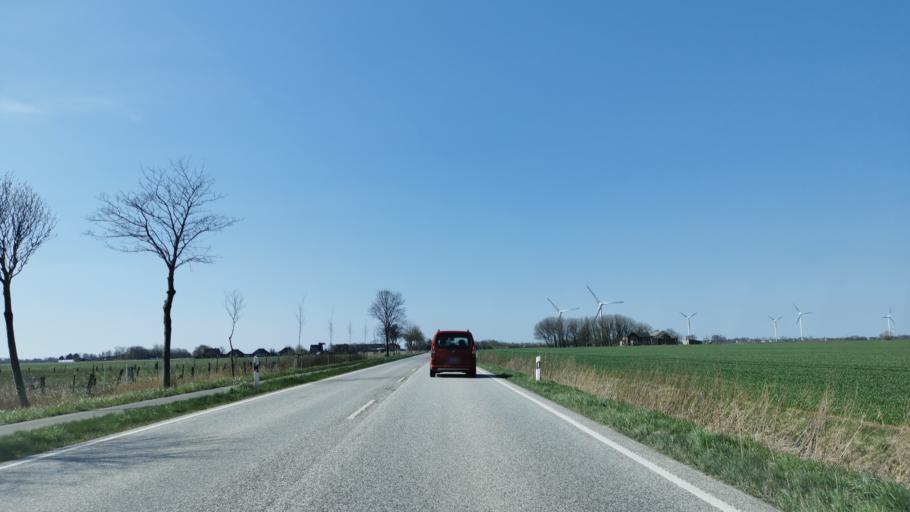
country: DE
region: Schleswig-Holstein
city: Friedrichsgabekoog
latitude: 54.1572
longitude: 8.9502
